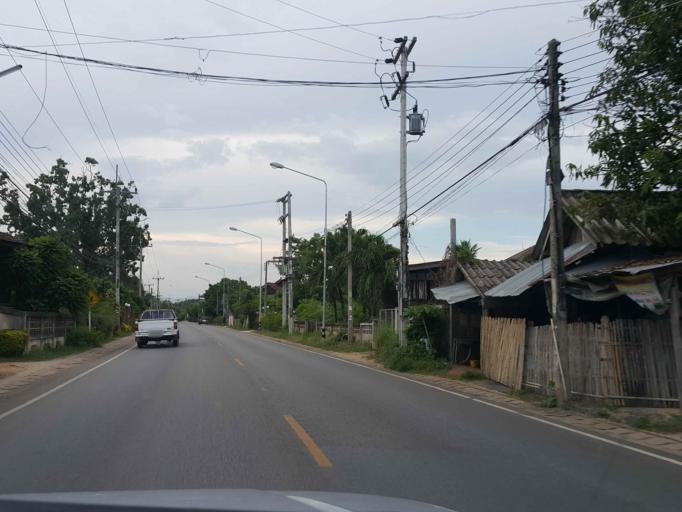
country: TH
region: Lampang
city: Ko Kha
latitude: 18.2476
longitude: 99.3889
